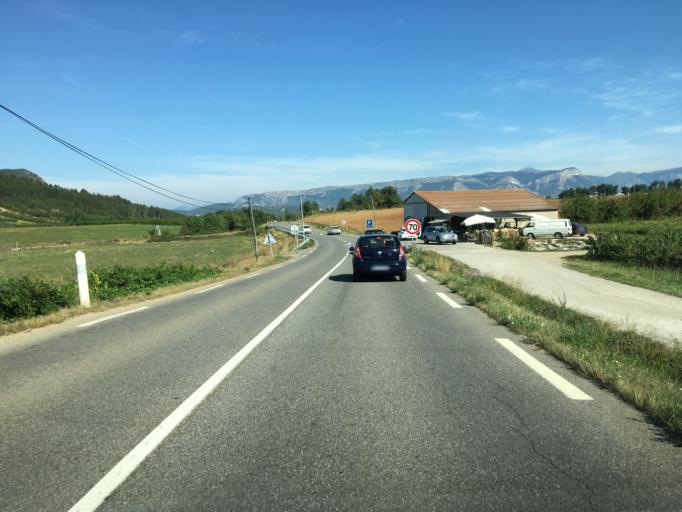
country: FR
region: Provence-Alpes-Cote d'Azur
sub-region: Departement des Hautes-Alpes
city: Laragne-Monteglin
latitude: 44.2807
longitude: 5.8481
